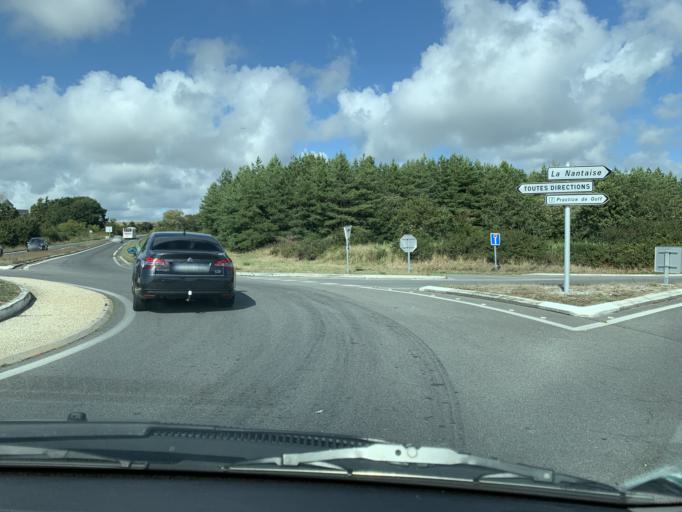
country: FR
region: Pays de la Loire
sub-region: Departement de la Loire-Atlantique
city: Guerande
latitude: 47.3147
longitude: -2.4285
